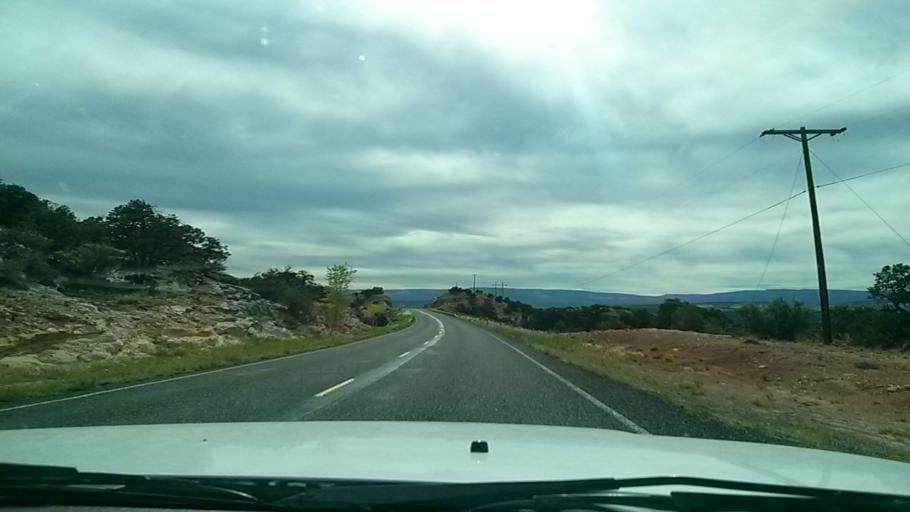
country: US
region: Utah
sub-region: Wayne County
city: Loa
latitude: 37.7507
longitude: -111.4627
